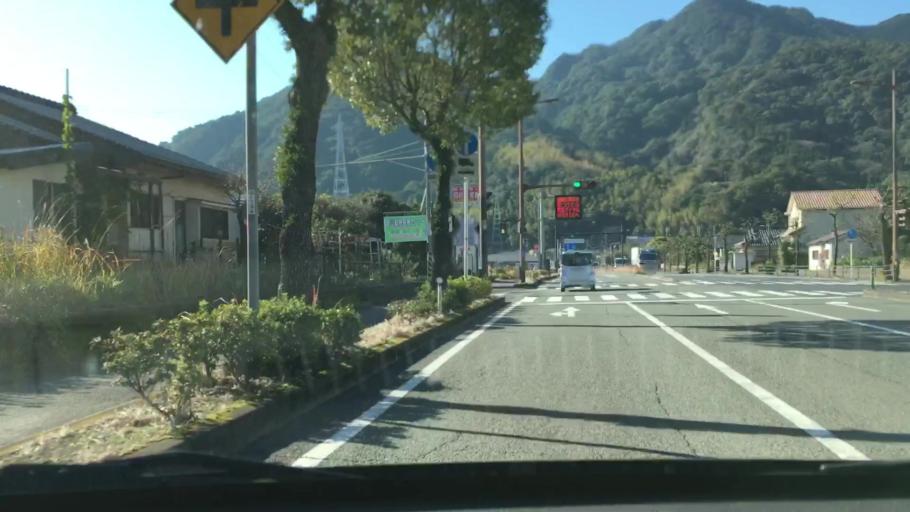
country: JP
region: Kagoshima
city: Kajiki
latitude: 31.7066
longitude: 130.6139
